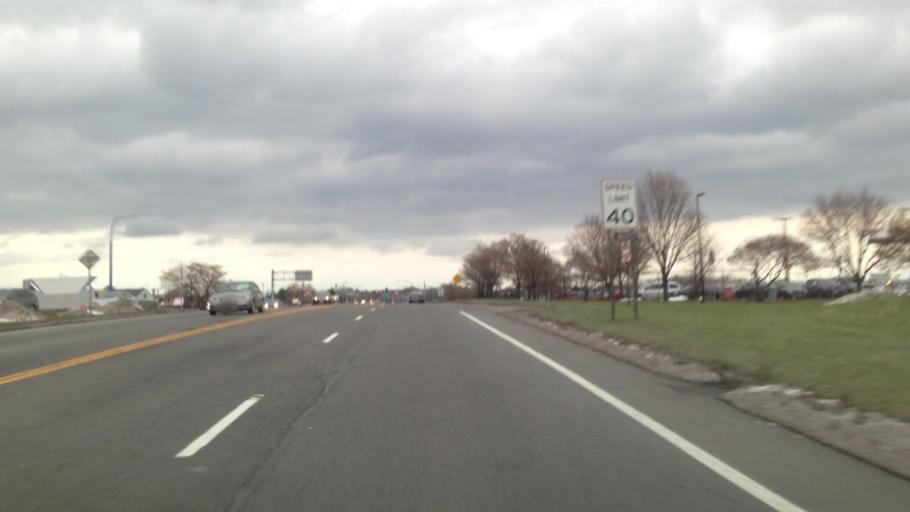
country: US
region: New York
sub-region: Monroe County
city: North Gates
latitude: 43.1307
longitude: -77.6710
